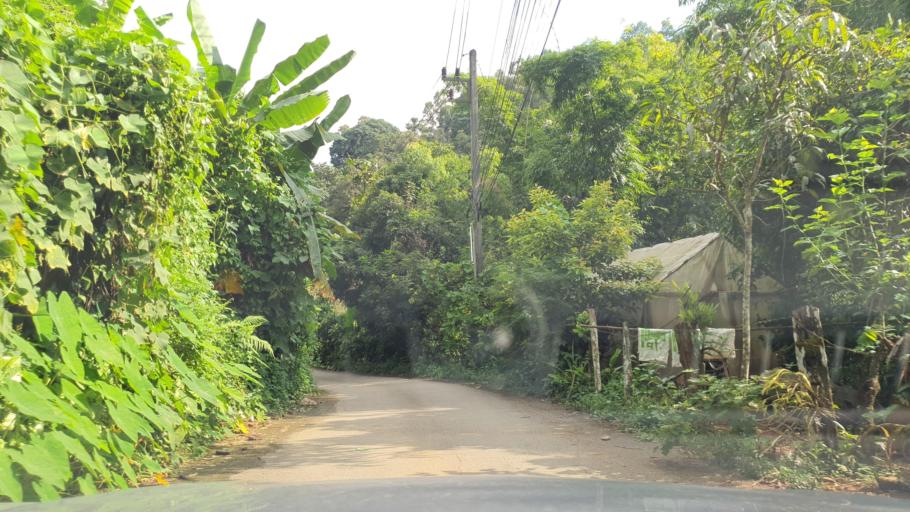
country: TH
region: Chiang Mai
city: Mae On
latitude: 18.9386
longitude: 99.3094
